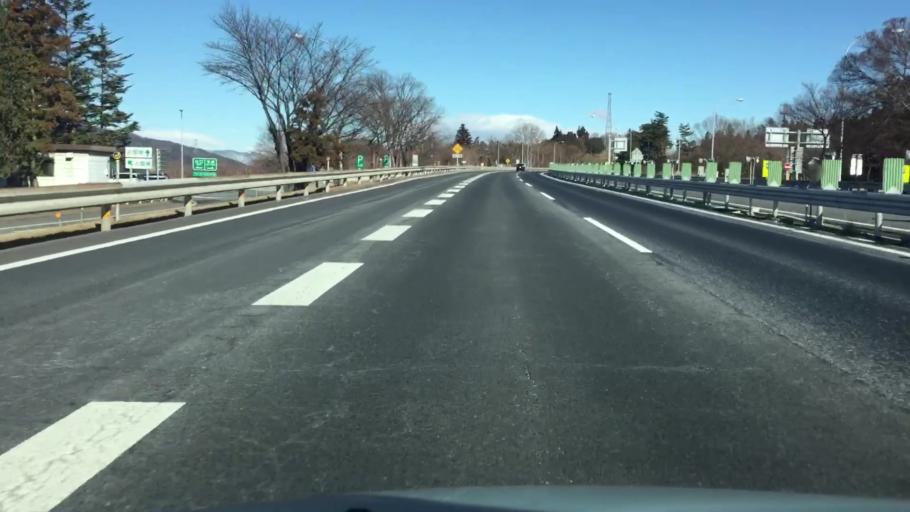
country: JP
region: Gunma
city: Shibukawa
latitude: 36.5369
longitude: 139.0481
